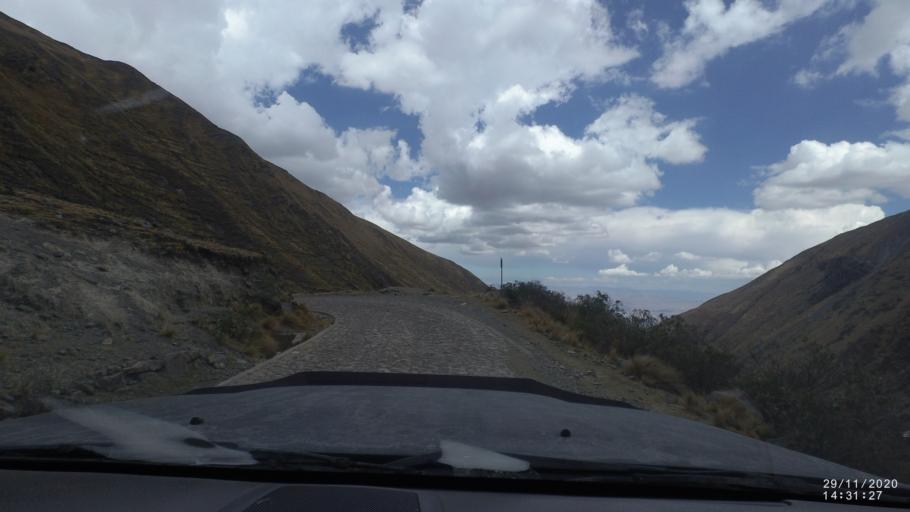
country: BO
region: Cochabamba
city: Sipe Sipe
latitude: -17.2665
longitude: -66.3445
